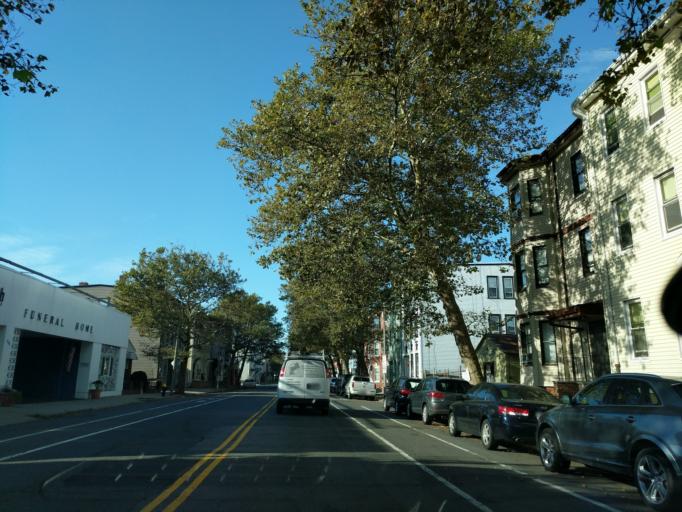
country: US
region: Massachusetts
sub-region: Suffolk County
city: Chelsea
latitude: 42.3779
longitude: -71.0295
